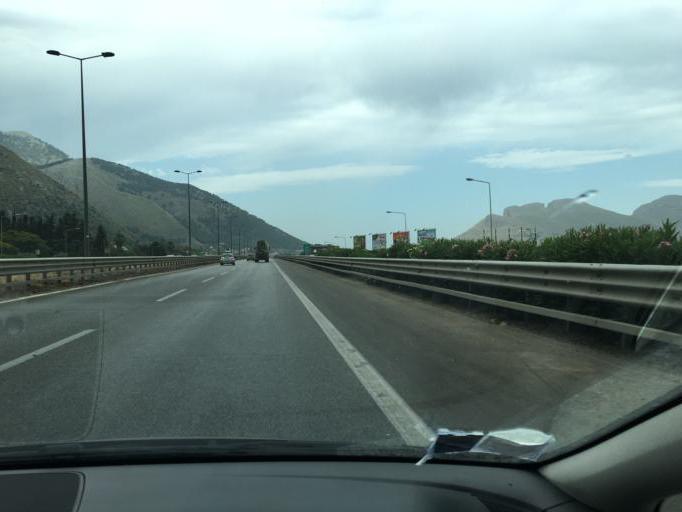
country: IT
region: Sicily
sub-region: Palermo
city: Palermo
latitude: 38.1635
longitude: 13.3083
